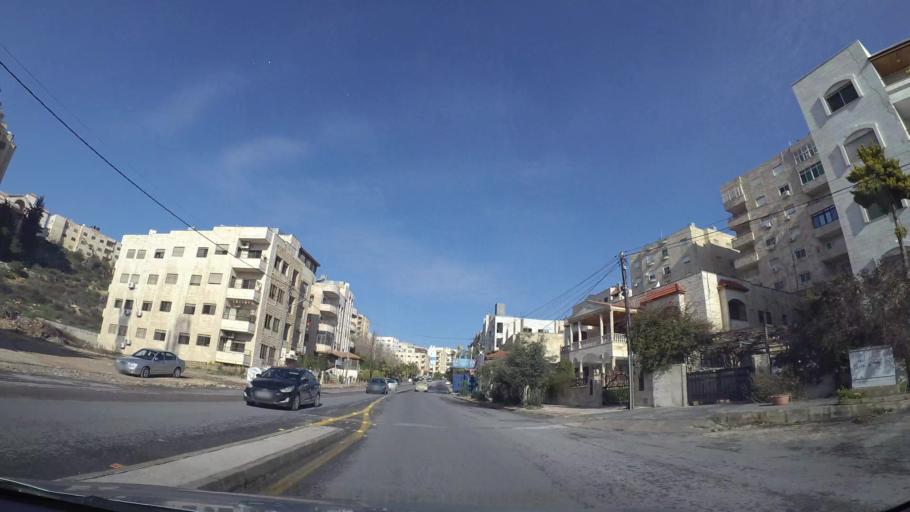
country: JO
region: Amman
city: Al Jubayhah
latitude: 32.0018
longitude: 35.8551
